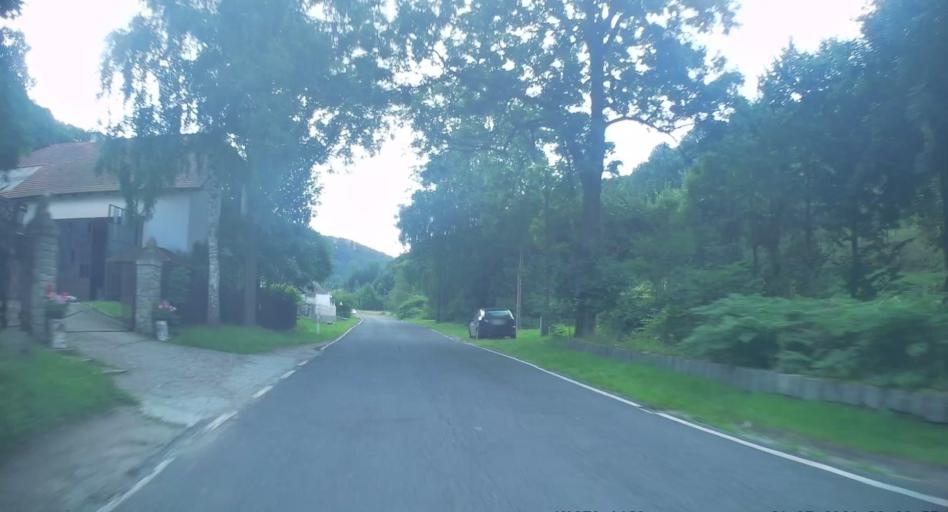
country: PL
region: Lower Silesian Voivodeship
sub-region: Powiat walbrzyski
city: Walim
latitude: 50.7166
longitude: 16.4248
